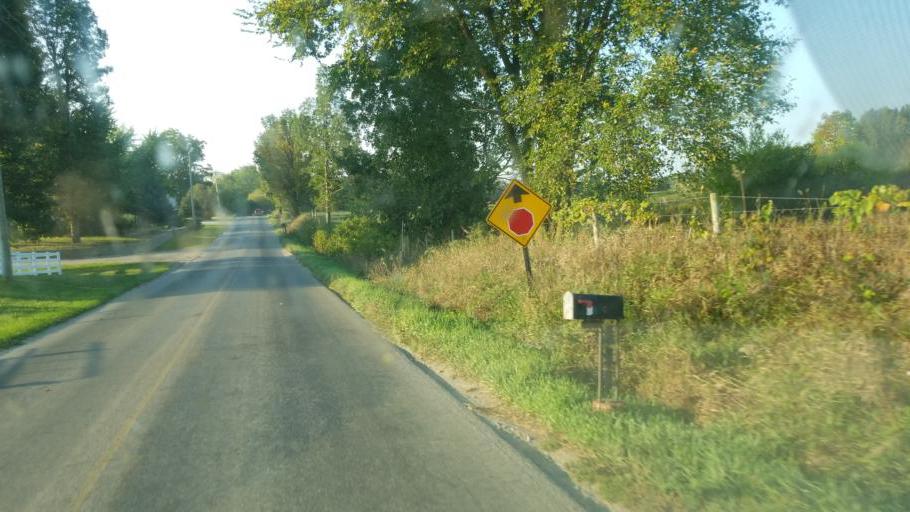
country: US
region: Indiana
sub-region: LaGrange County
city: Lagrange
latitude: 41.5785
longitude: -85.4240
